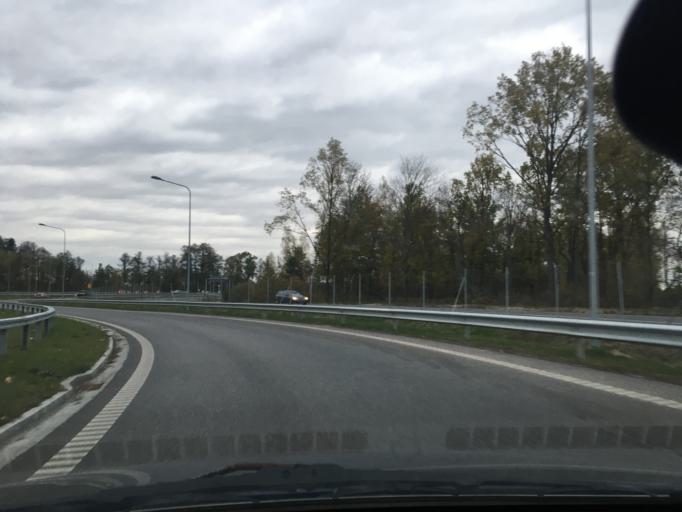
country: PL
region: Lodz Voivodeship
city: Zabia Wola
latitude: 52.0508
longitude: 20.7217
